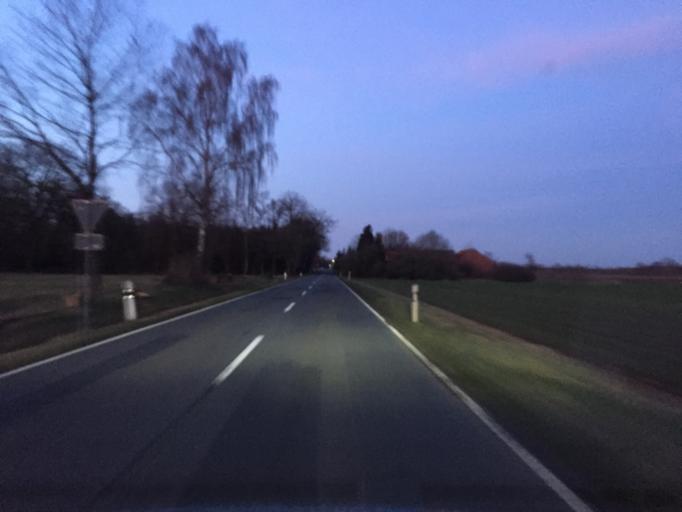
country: DE
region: Lower Saxony
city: Kirchdorf
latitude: 52.6104
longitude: 8.8949
